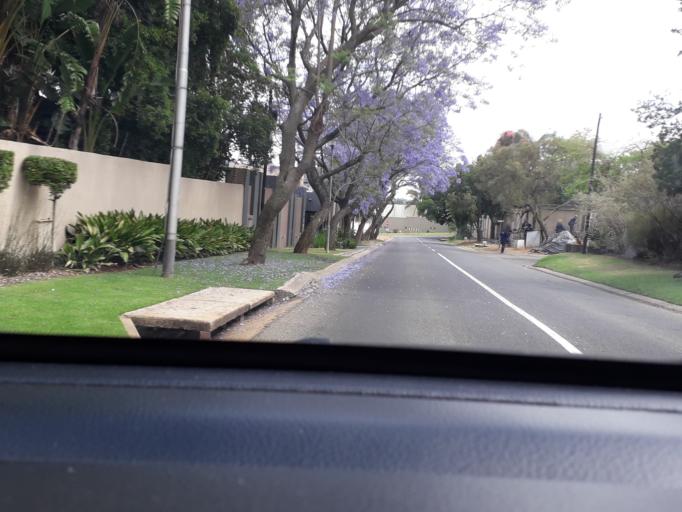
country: ZA
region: Gauteng
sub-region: City of Johannesburg Metropolitan Municipality
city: Midrand
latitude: -26.0703
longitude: 28.0543
